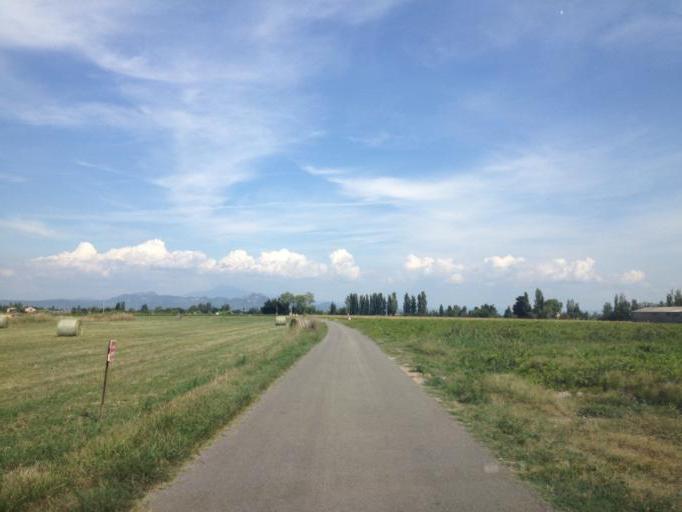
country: FR
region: Provence-Alpes-Cote d'Azur
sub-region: Departement du Vaucluse
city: Camaret-sur-Aigues
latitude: 44.1515
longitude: 4.8474
